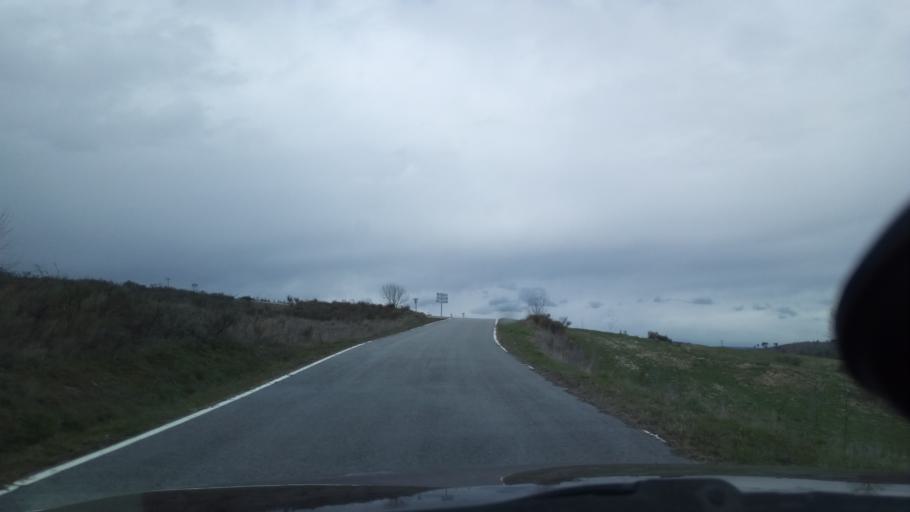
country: PT
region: Guarda
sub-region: Fornos de Algodres
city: Fornos de Algodres
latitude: 40.5720
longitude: -7.4689
